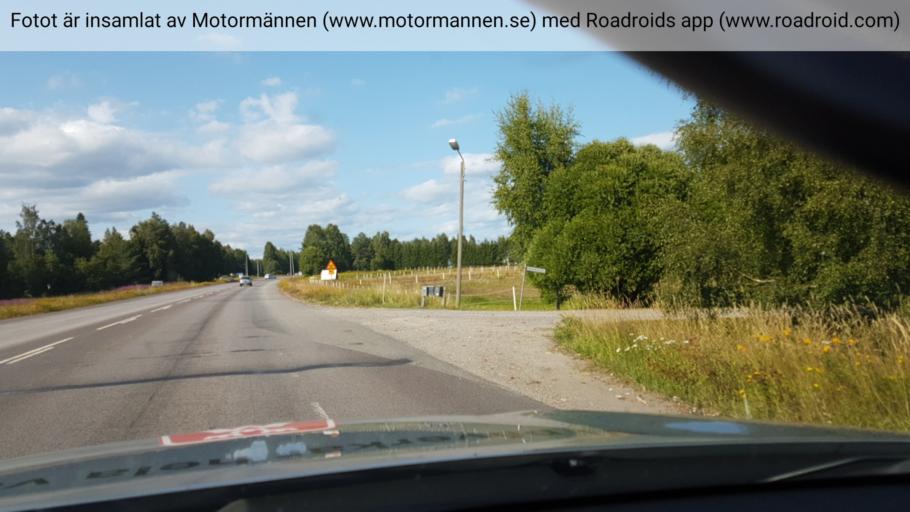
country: SE
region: Norrbotten
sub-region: Pitea Kommun
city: Pitea
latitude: 65.2836
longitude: 21.5085
